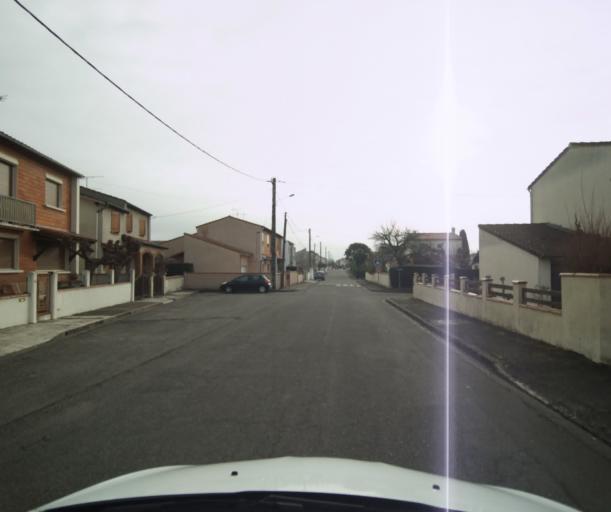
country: FR
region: Midi-Pyrenees
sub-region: Departement du Tarn-et-Garonne
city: Castelsarrasin
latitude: 44.0336
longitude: 1.1141
